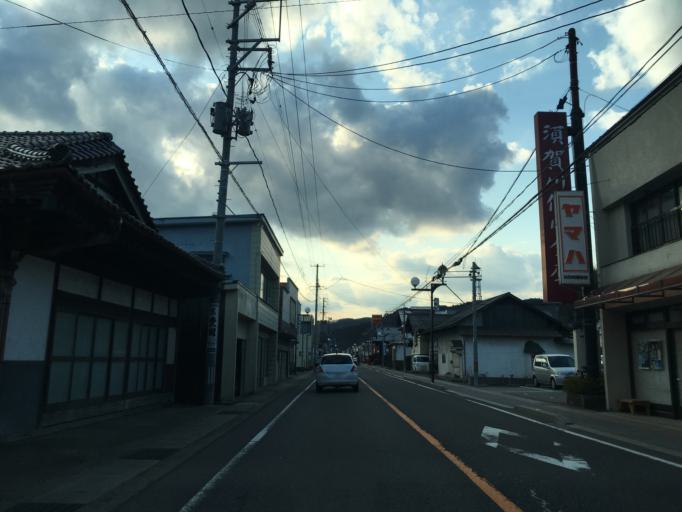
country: JP
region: Fukushima
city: Ishikawa
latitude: 37.0922
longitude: 140.5518
